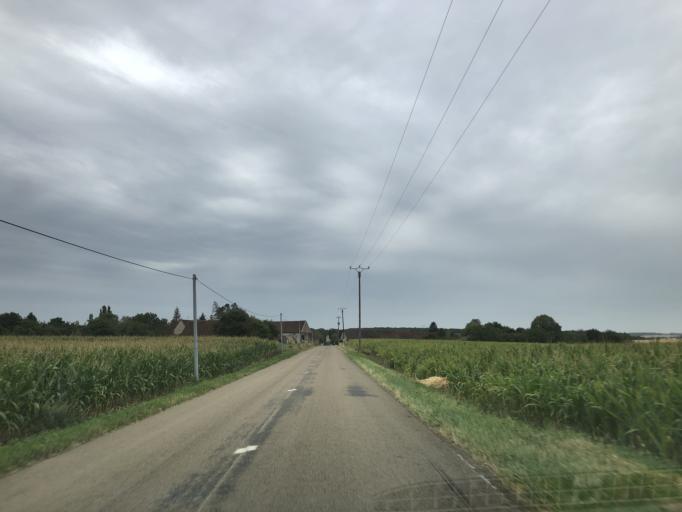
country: FR
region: Centre
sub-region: Departement du Loiret
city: Douchy
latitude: 47.9762
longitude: 3.1427
